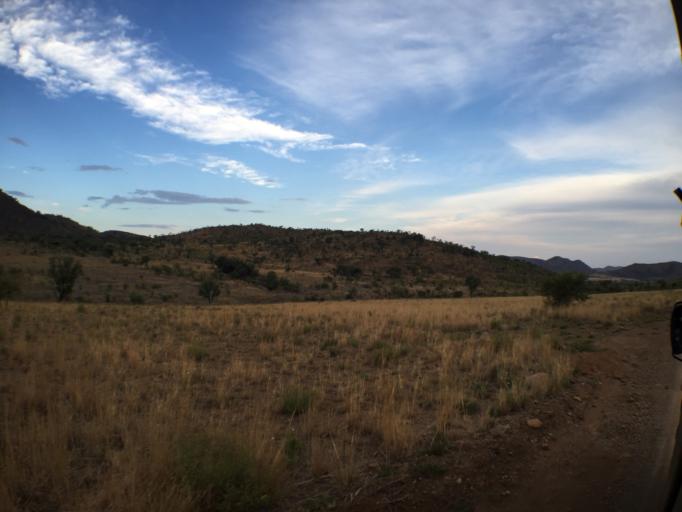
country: ZA
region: North-West
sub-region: Bojanala Platinum District Municipality
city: Mogwase
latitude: -25.2262
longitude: 27.0807
